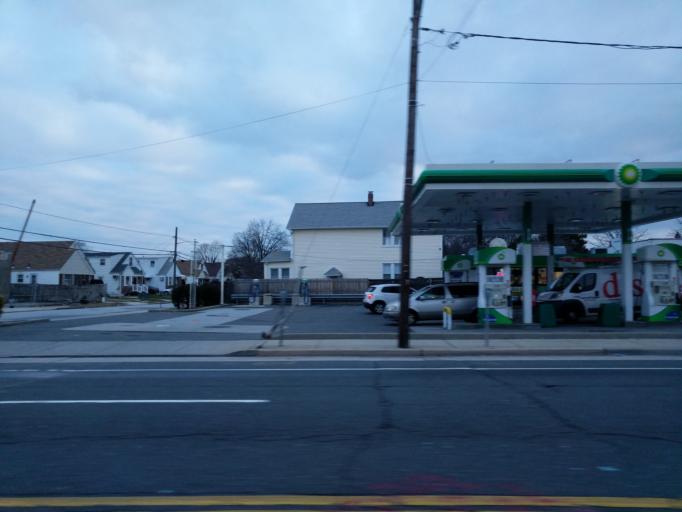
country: US
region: New York
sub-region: Nassau County
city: Valley Stream
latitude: 40.6684
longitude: -73.7114
